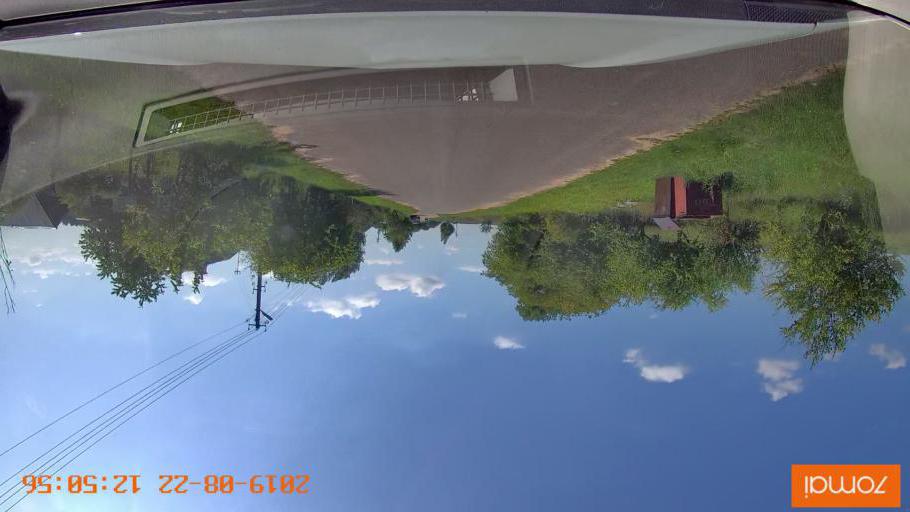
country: BY
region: Minsk
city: Prawdzinski
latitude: 53.4603
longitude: 27.6480
